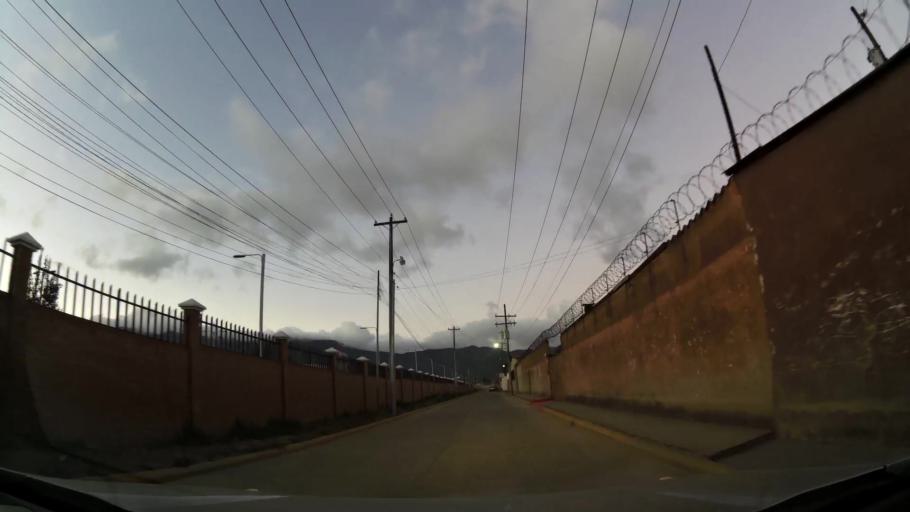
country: GT
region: Quetzaltenango
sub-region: Municipio de La Esperanza
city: La Esperanza
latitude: 14.8602
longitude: -91.5484
